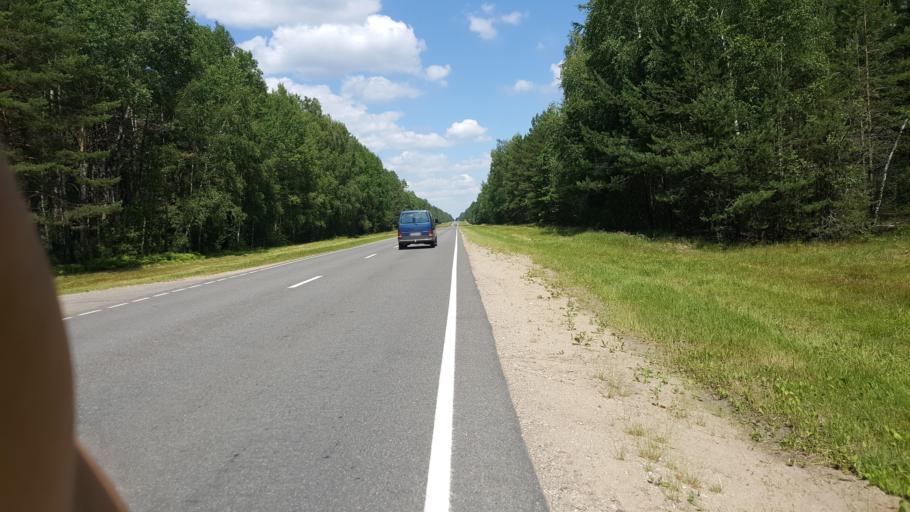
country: BY
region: Brest
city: Kamyanyuki
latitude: 52.5130
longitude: 23.7889
